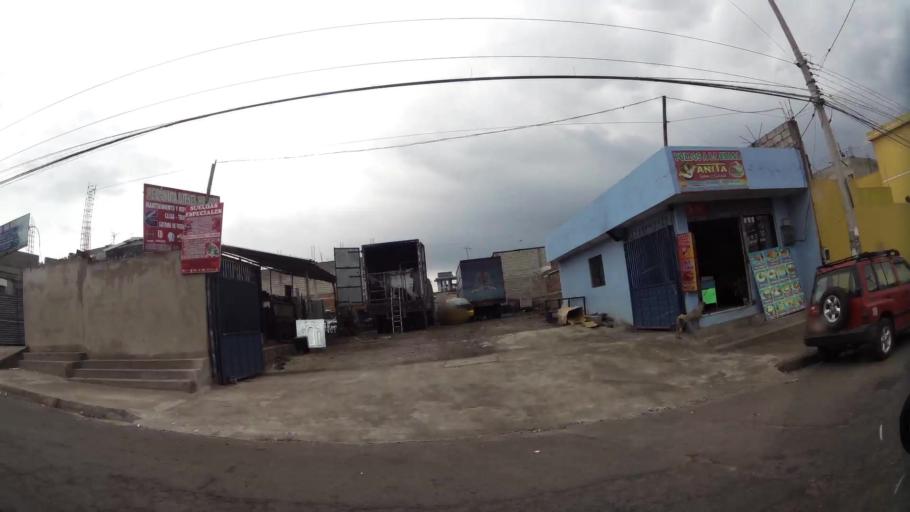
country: EC
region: Pichincha
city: Sangolqui
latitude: -0.3550
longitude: -78.5497
